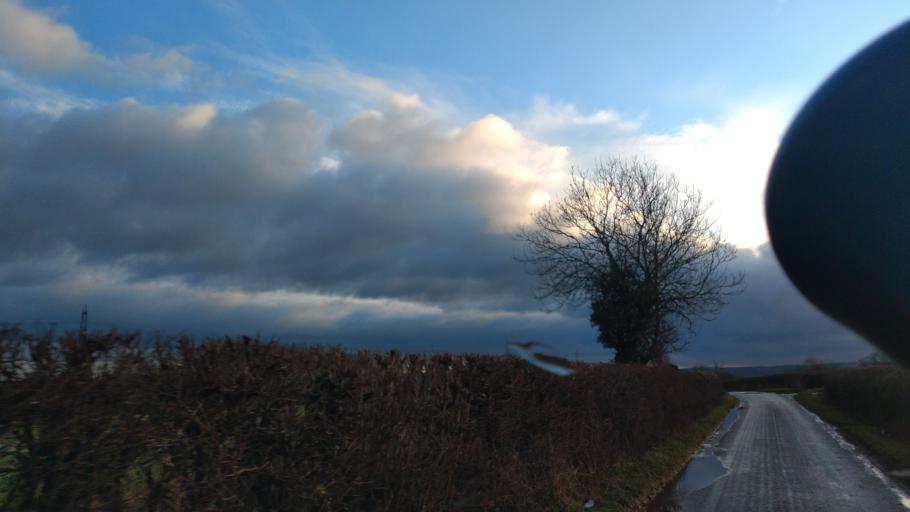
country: GB
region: England
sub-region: Wiltshire
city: Biddestone
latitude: 51.4539
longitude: -2.1833
